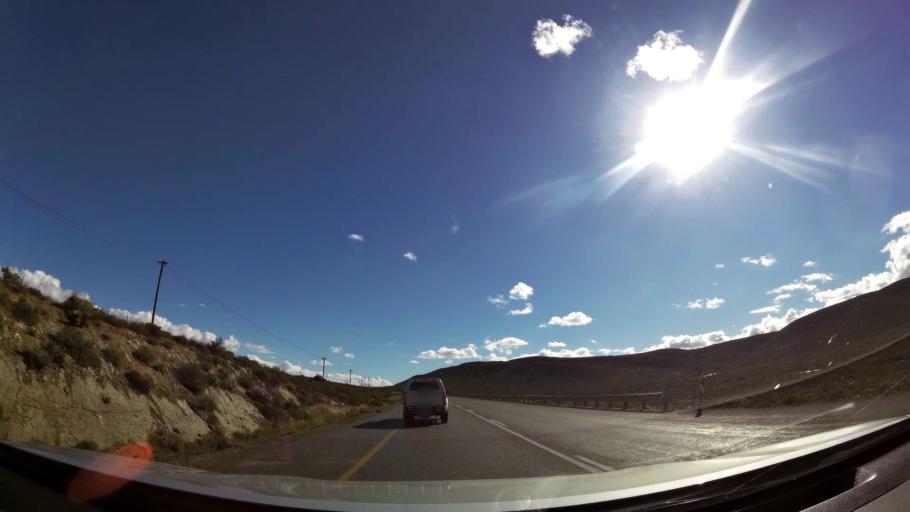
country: ZA
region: Western Cape
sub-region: Cape Winelands District Municipality
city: Worcester
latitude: -33.7353
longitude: 19.6727
